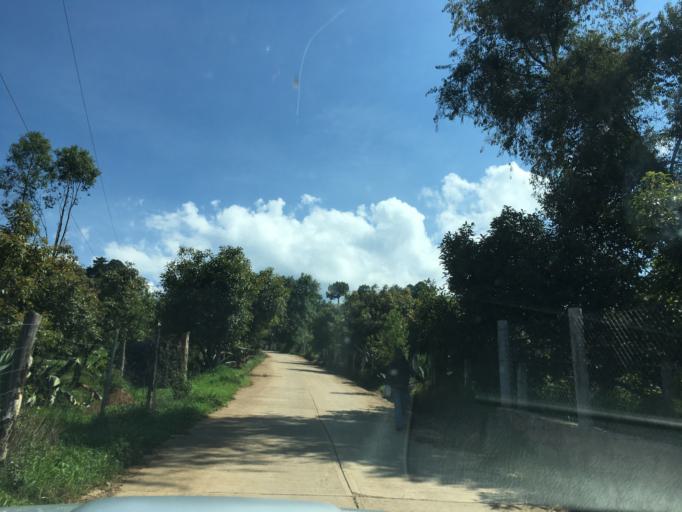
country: MX
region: Michoacan
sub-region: Zitacuaro
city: La Fundicion (Quinta Manzana)
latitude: 19.4878
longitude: -100.3117
